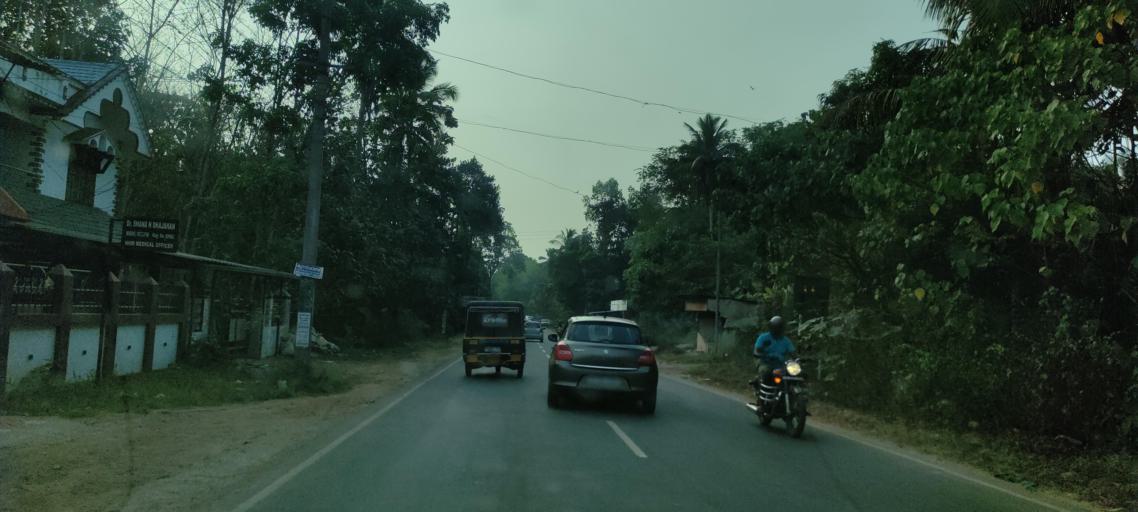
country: IN
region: Kerala
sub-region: Pattanamtitta
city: Adur
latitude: 9.1669
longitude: 76.6759
